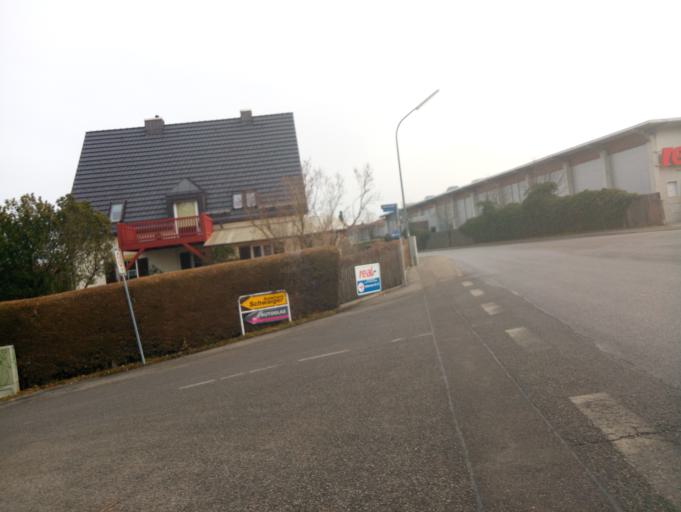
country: DE
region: Bavaria
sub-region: Upper Bavaria
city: Weilheim
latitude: 47.8440
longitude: 11.1492
